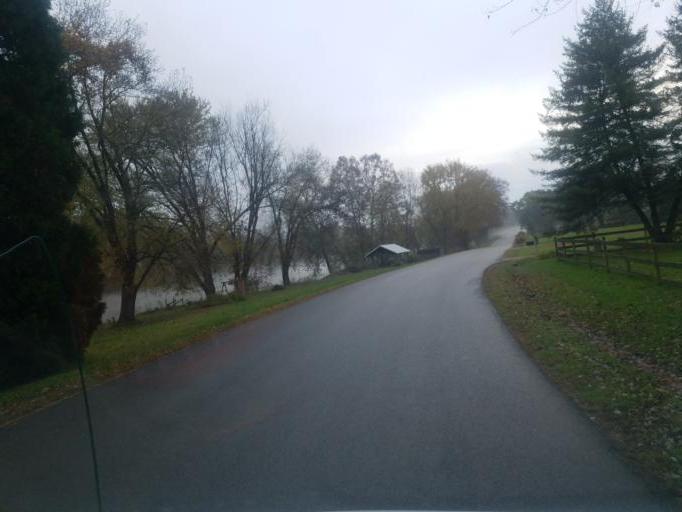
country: US
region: Ohio
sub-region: Morgan County
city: McConnelsville
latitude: 39.5383
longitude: -81.7843
